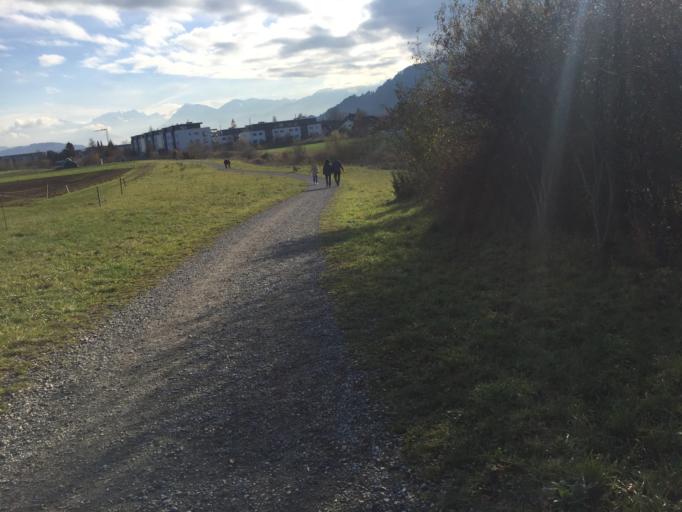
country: CH
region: Bern
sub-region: Bern-Mittelland District
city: Munsingen
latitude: 46.8793
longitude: 7.5485
